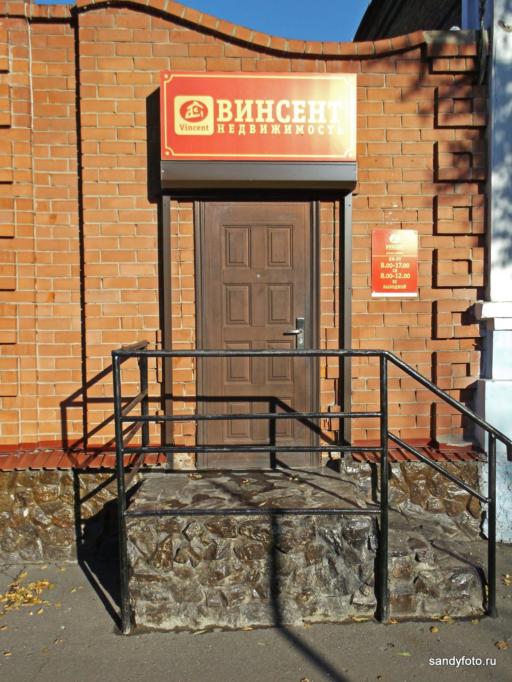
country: RU
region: Chelyabinsk
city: Troitsk
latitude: 54.0836
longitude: 61.5550
